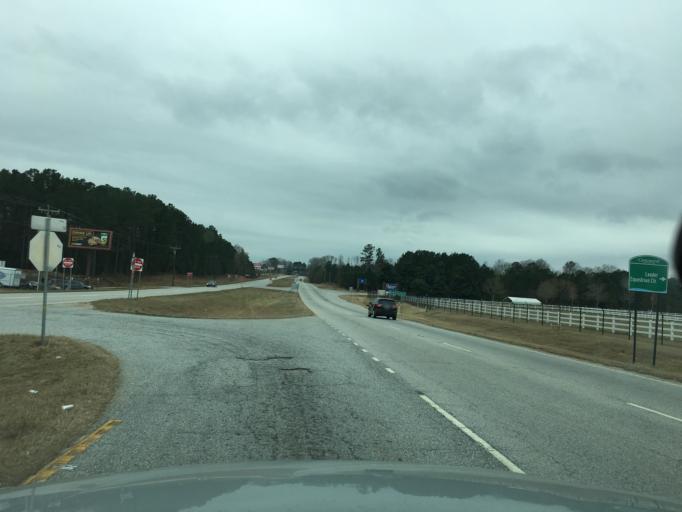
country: US
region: South Carolina
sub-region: Greenwood County
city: Greenwood
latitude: 34.2342
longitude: -82.1039
